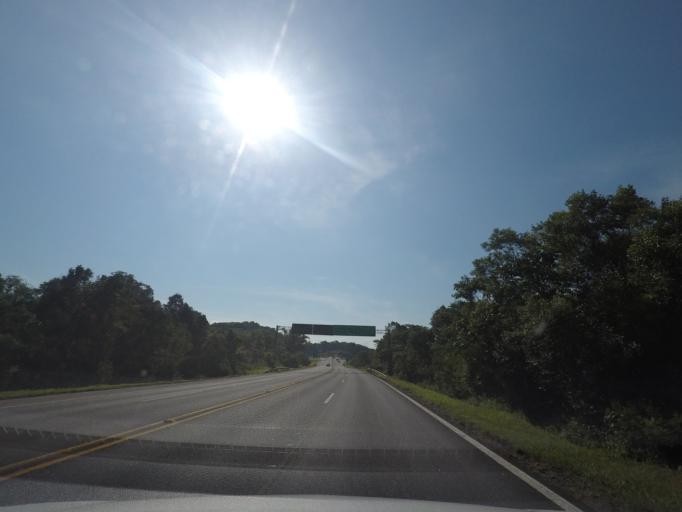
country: BR
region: Parana
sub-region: Paranagua
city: Paranagua
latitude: -25.5729
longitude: -48.6132
